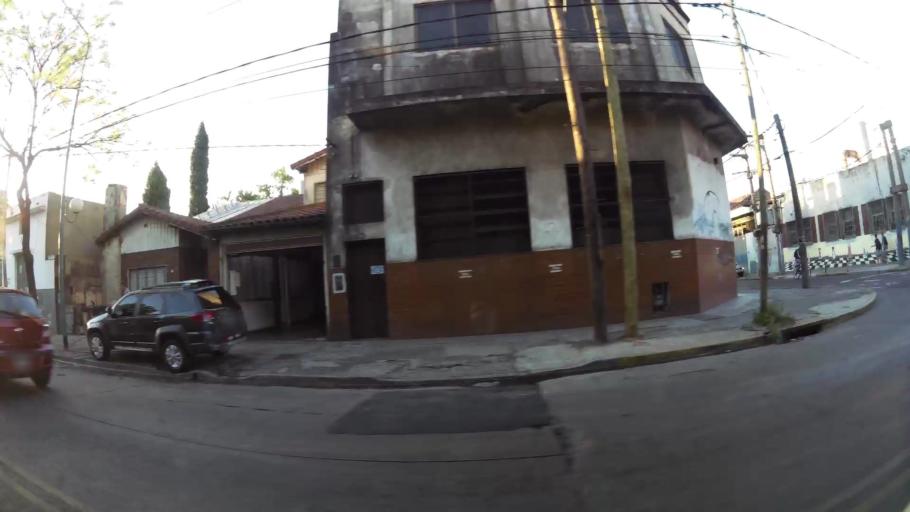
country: AR
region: Buenos Aires
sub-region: Partido de General San Martin
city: General San Martin
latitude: -34.5523
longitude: -58.5138
